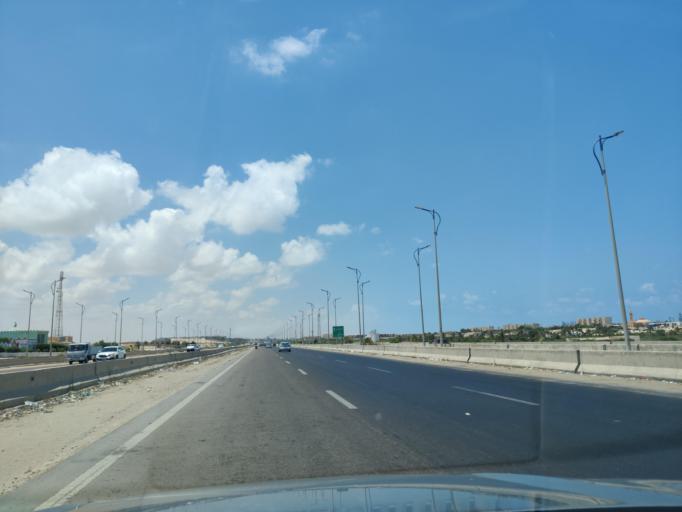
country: EG
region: Muhafazat Matruh
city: Al `Alamayn
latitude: 30.8965
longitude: 29.4058
